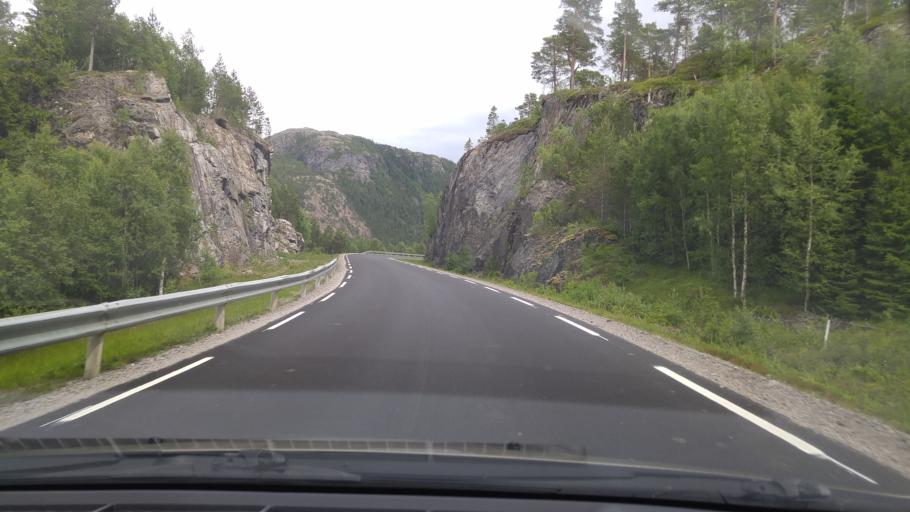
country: NO
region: Nord-Trondelag
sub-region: Namsos
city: Namsos
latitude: 64.5925
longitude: 11.4460
